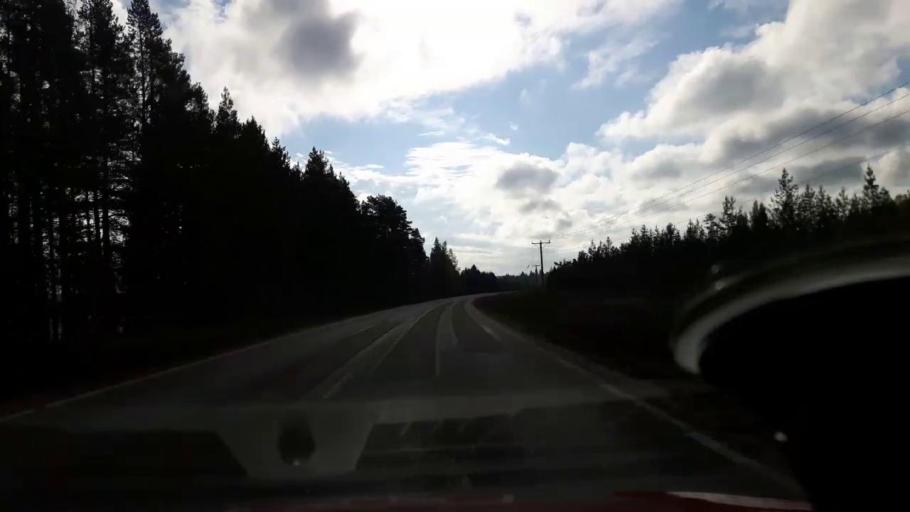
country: SE
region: Jaemtland
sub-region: Harjedalens Kommun
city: Sveg
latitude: 62.1107
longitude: 15.0595
